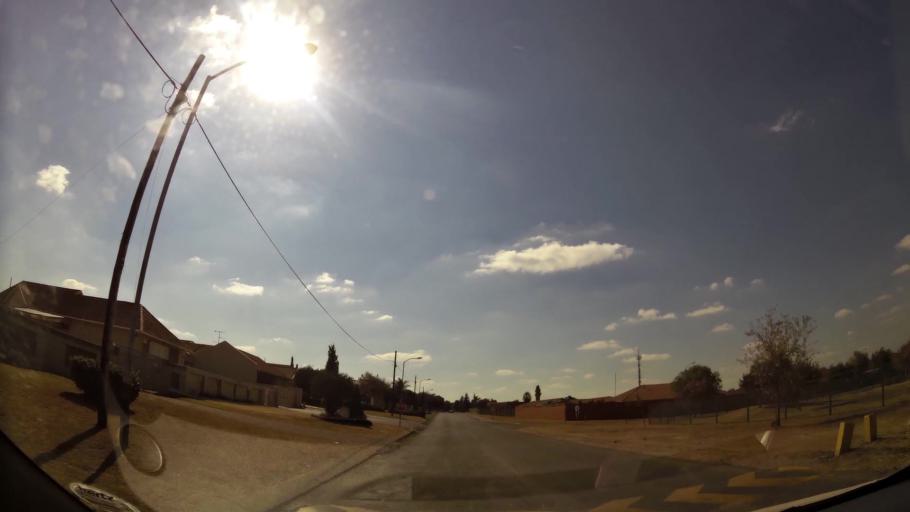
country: ZA
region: Gauteng
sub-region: West Rand District Municipality
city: Randfontein
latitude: -26.1711
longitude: 27.7474
